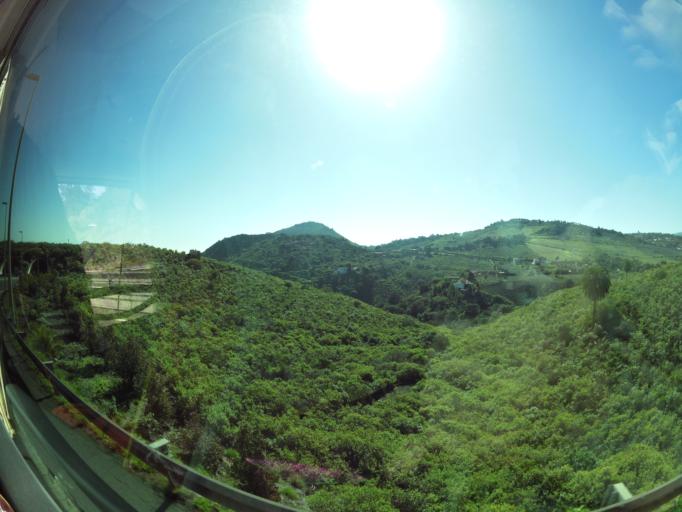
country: ES
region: Canary Islands
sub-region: Provincia de Las Palmas
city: Santa Brigida
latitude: 28.0472
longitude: -15.4715
